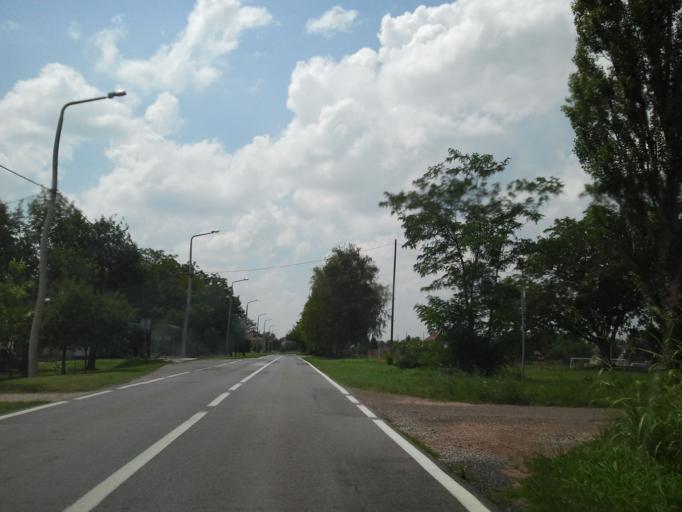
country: HR
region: Vukovarsko-Srijemska
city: Lovas
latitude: 45.2890
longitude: 19.1073
